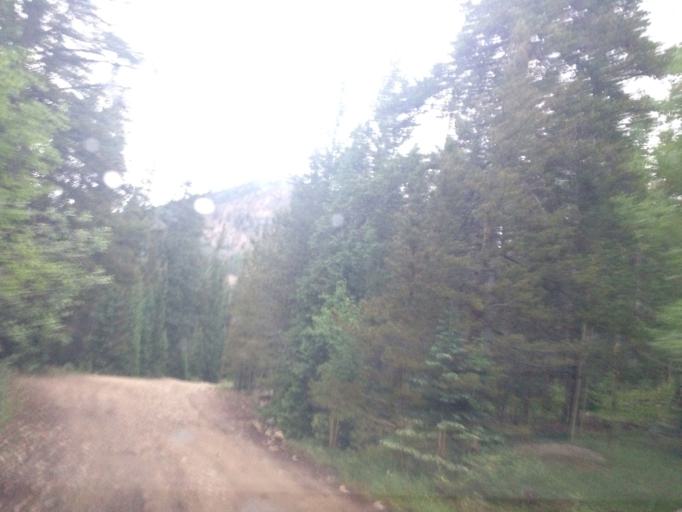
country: US
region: Colorado
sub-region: Clear Creek County
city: Georgetown
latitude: 39.5623
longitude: -105.7653
